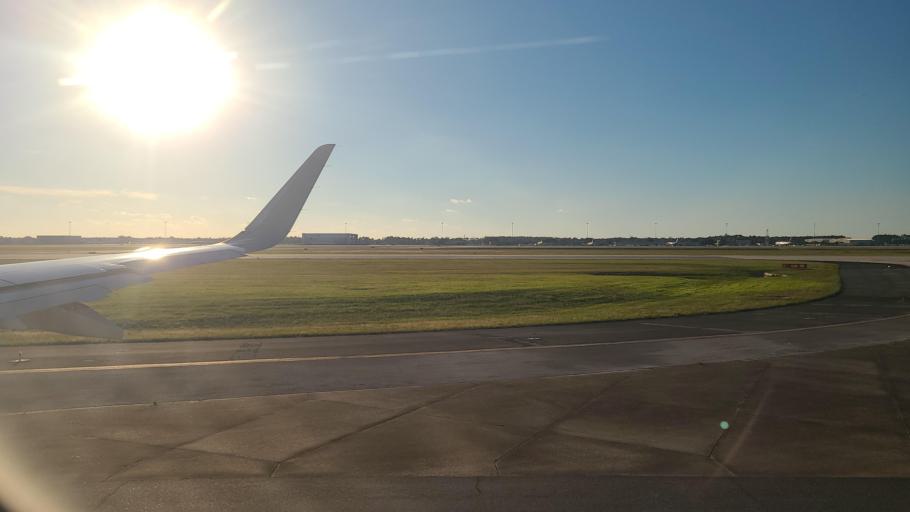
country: US
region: Florida
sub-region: Orange County
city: Taft
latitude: 28.4263
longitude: -81.3199
